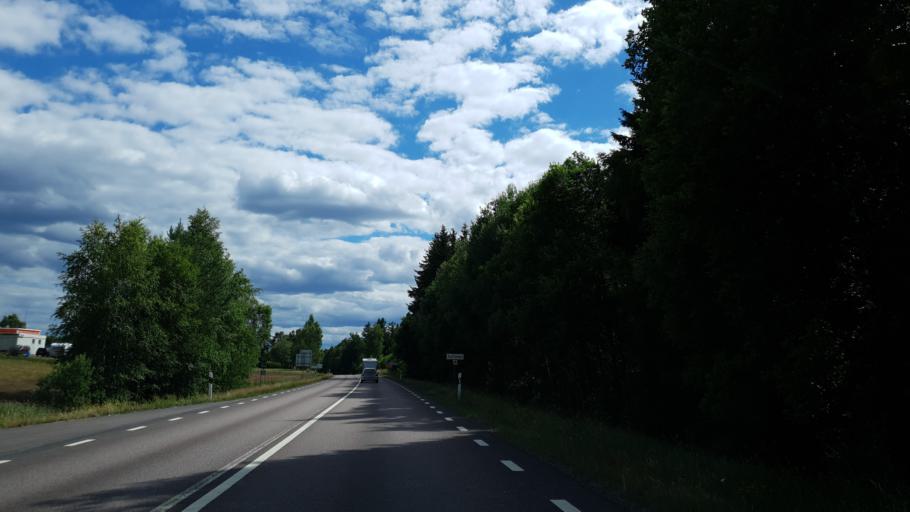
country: SE
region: Kronoberg
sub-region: Lessebo Kommun
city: Lessebo
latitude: 56.8468
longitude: 15.3890
